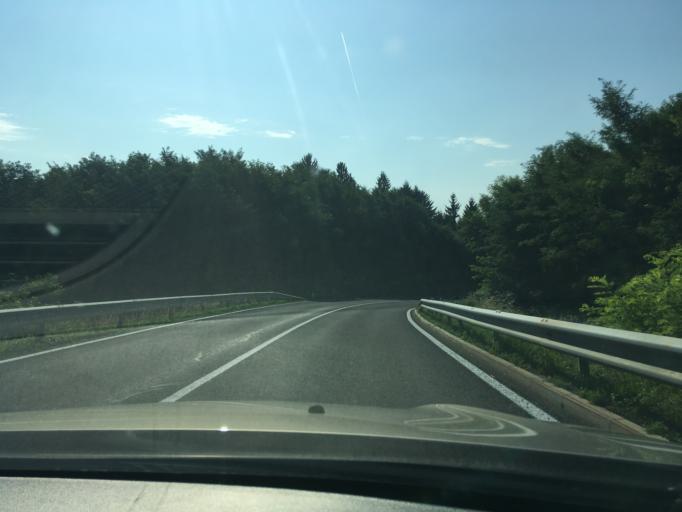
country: SI
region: Novo Mesto
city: Novo Mesto
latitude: 45.8395
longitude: 15.1578
